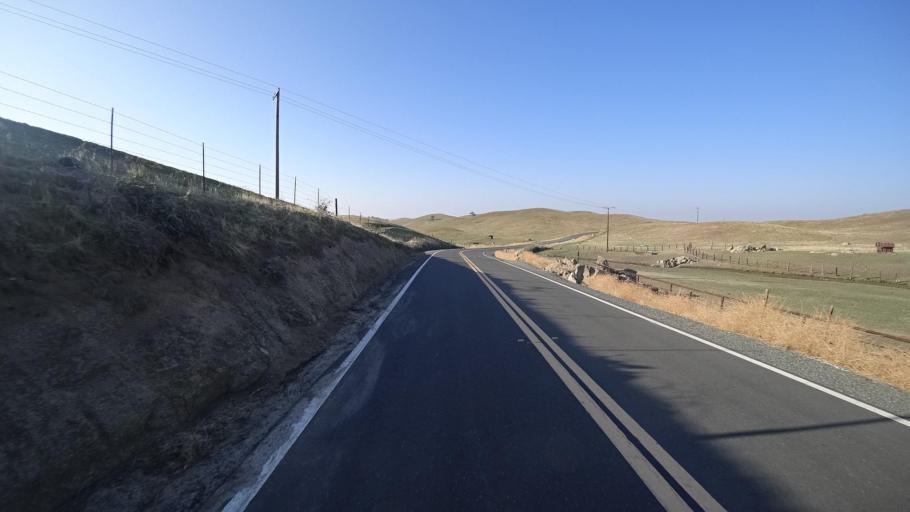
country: US
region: California
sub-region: Tulare County
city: Richgrove
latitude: 35.7425
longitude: -118.8839
